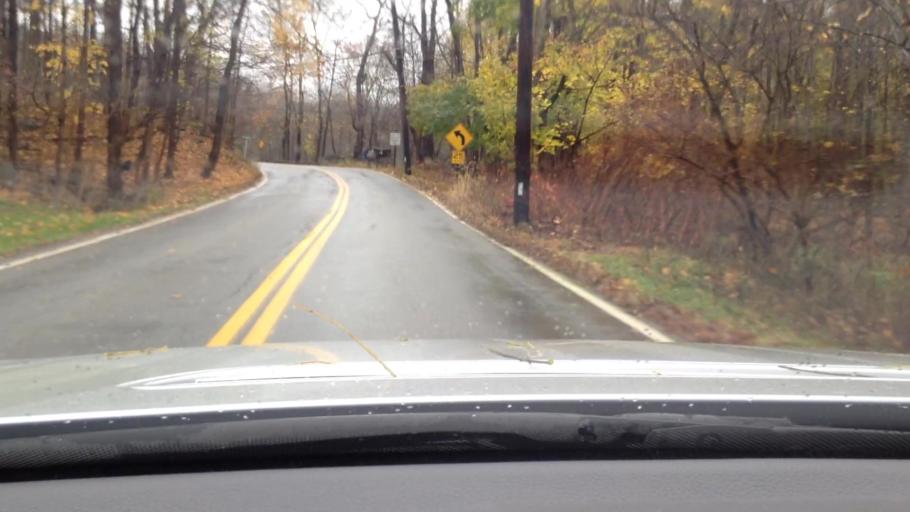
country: US
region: New York
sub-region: Westchester County
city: Croton-on-Hudson
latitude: 41.2350
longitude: -73.8921
